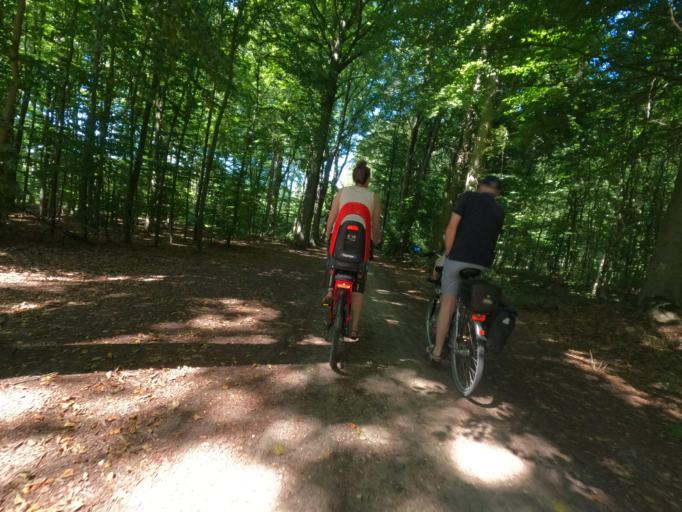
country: DE
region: North Rhine-Westphalia
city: Wegberg
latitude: 51.1427
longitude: 6.3103
